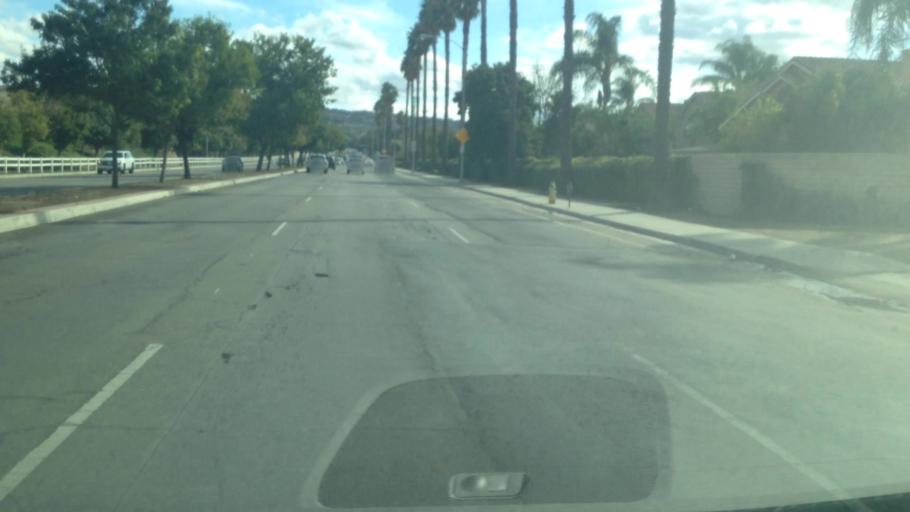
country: US
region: California
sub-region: Riverside County
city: Home Gardens
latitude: 33.8939
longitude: -117.4685
